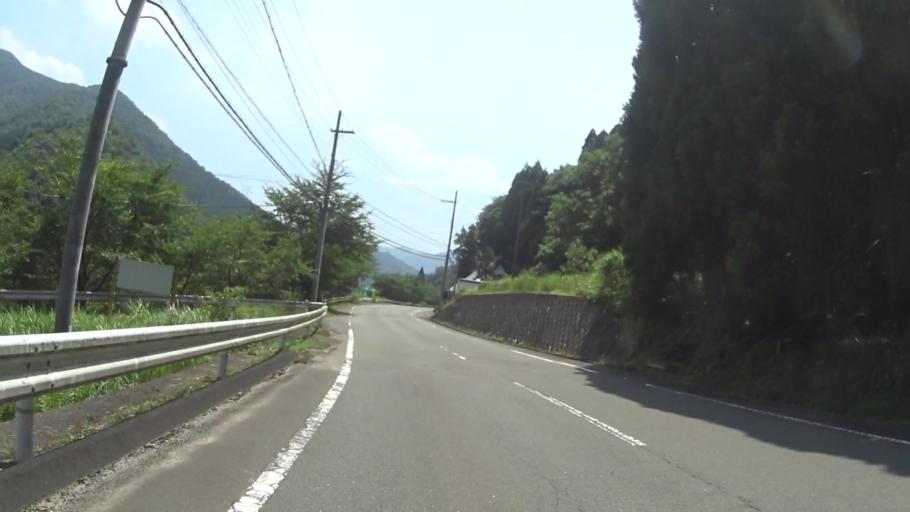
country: JP
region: Kyoto
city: Ayabe
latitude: 35.2845
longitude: 135.4285
